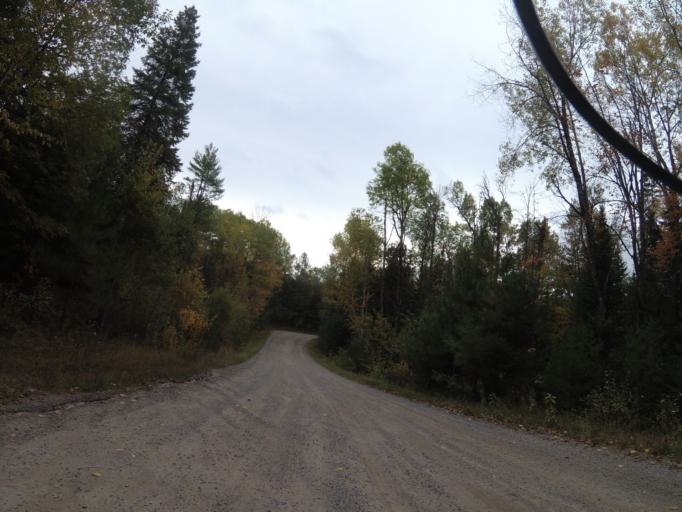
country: CA
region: Ontario
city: Renfrew
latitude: 45.2603
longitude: -77.1964
